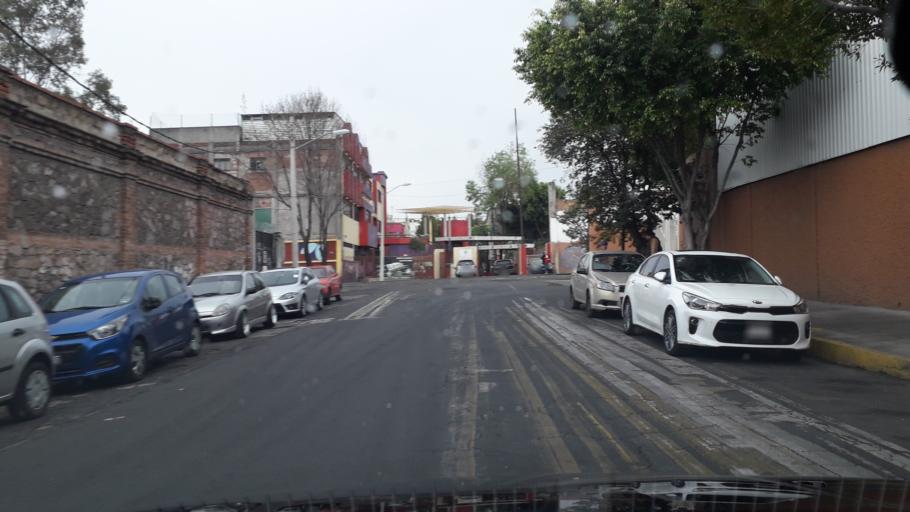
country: MX
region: Mexico City
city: Cuauhtemoc
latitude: 19.4565
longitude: -99.1596
